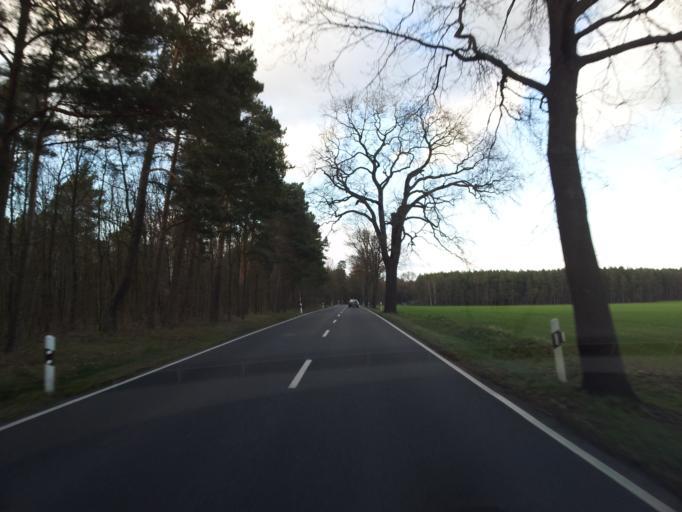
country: DE
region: Saxony
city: Konigsbruck
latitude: 51.3084
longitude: 13.9223
